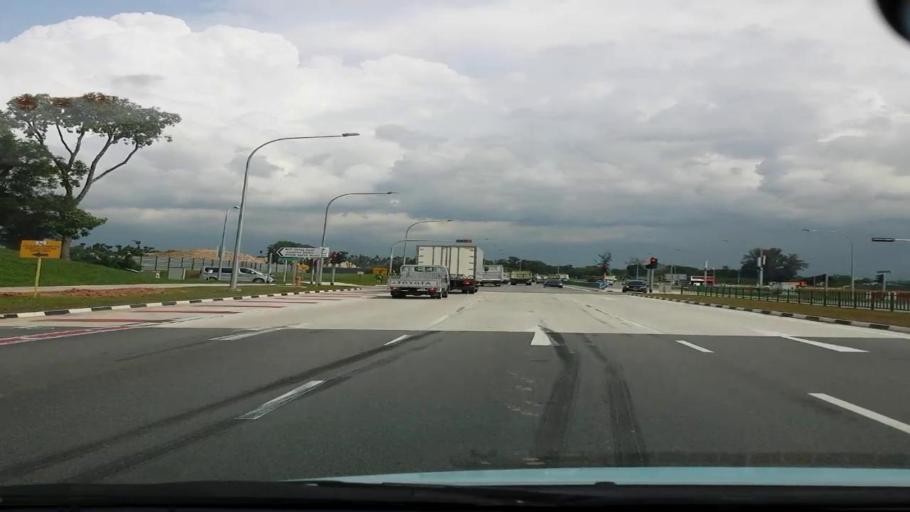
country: SG
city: Singapore
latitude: 1.3203
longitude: 103.9804
